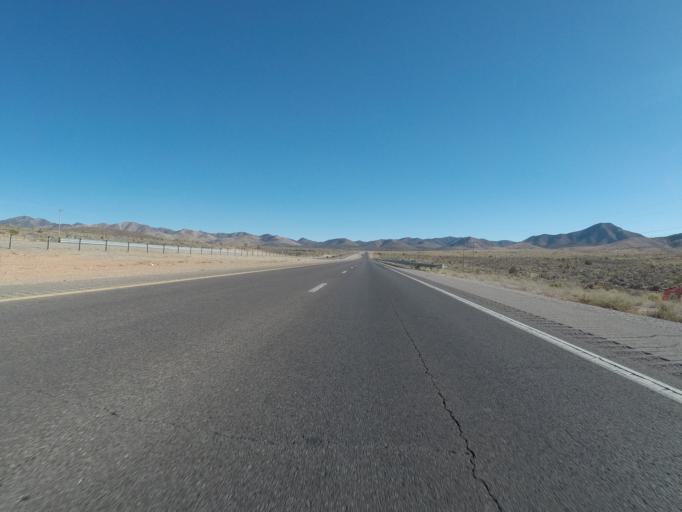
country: US
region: Nevada
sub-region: Clark County
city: Sandy Valley
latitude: 36.0149
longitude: -115.5685
